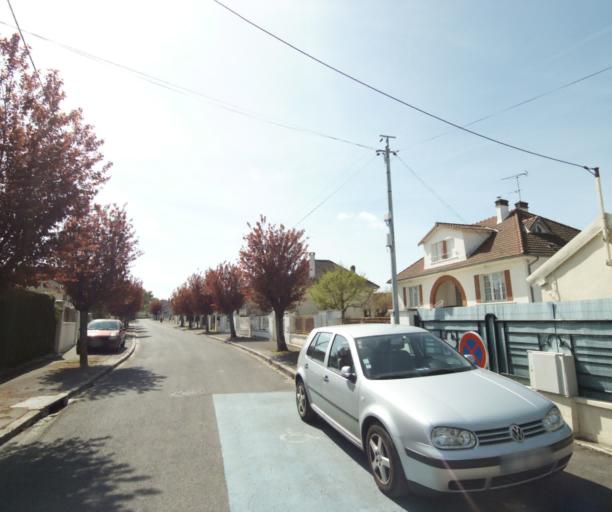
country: FR
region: Ile-de-France
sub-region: Departement de Seine-et-Marne
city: Nangis
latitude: 48.5574
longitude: 3.0189
